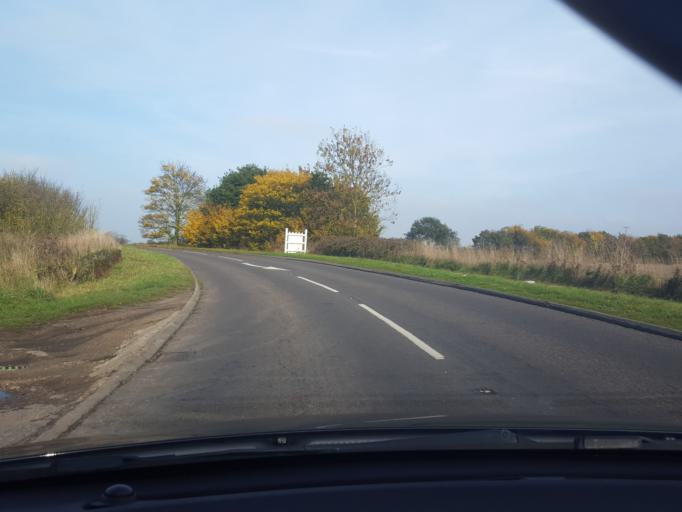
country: GB
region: England
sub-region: Essex
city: Mistley
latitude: 51.9133
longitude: 1.1585
